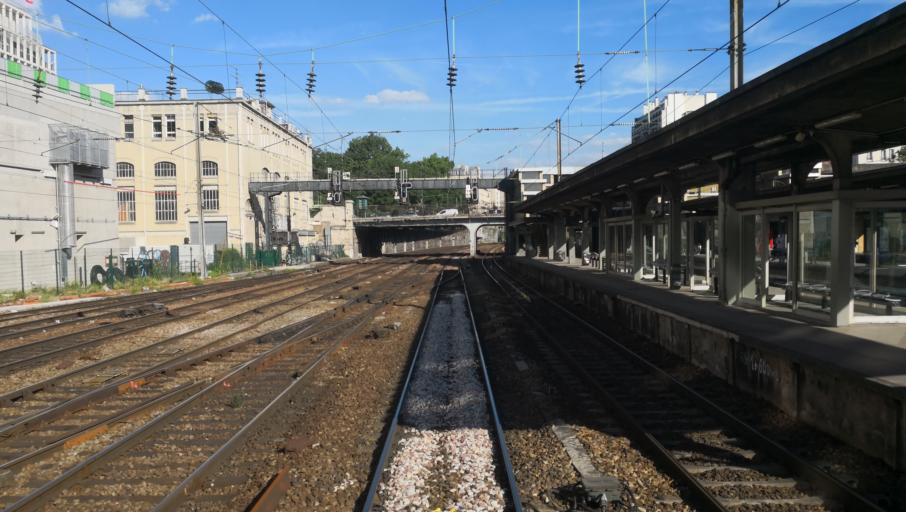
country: FR
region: Ile-de-France
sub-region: Paris
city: Saint-Ouen
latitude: 48.8826
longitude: 2.3334
